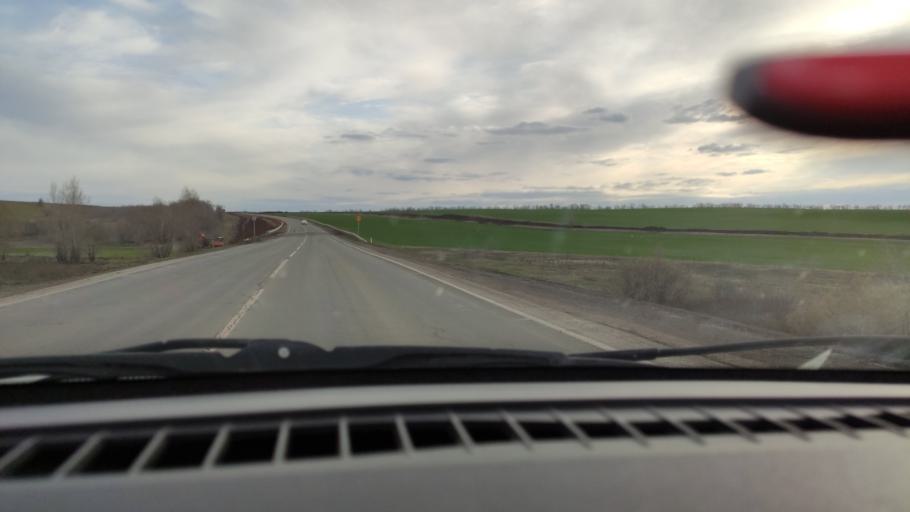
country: RU
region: Orenburg
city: Sakmara
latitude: 52.1880
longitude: 55.2975
